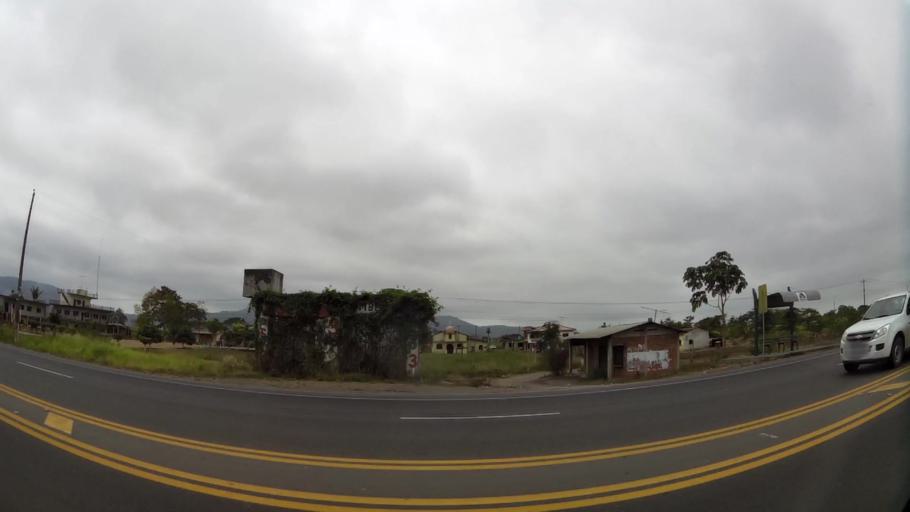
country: EC
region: Guayas
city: Naranjal
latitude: -2.4928
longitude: -79.6046
